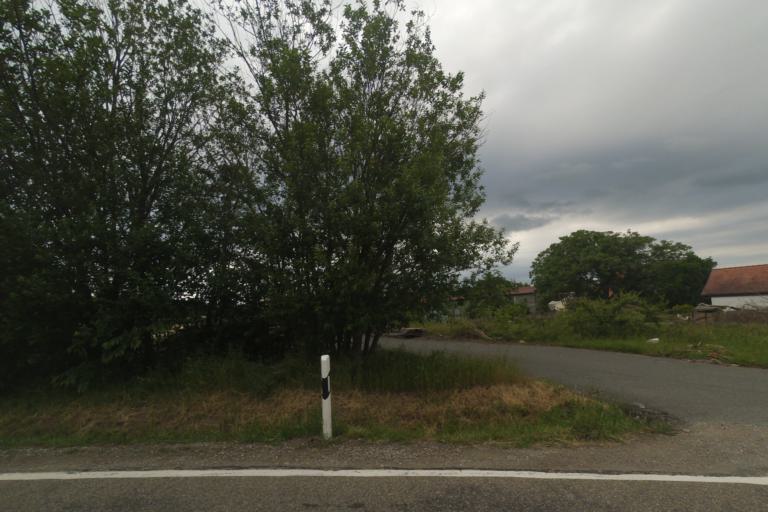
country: DE
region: Bavaria
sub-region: Regierungsbezirk Mittelfranken
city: Burghaslach
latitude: 49.7105
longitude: 10.6043
